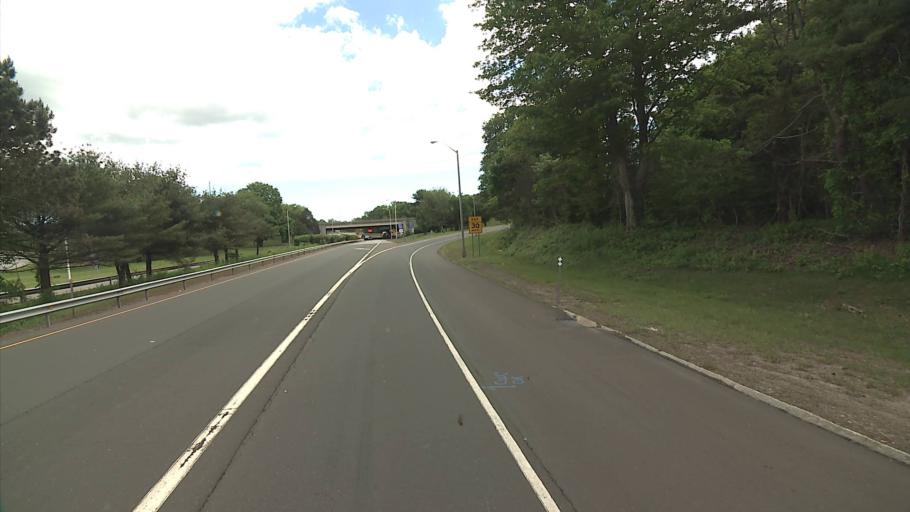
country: US
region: Connecticut
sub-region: Middlesex County
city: Old Saybrook Center
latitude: 41.3177
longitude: -72.3610
